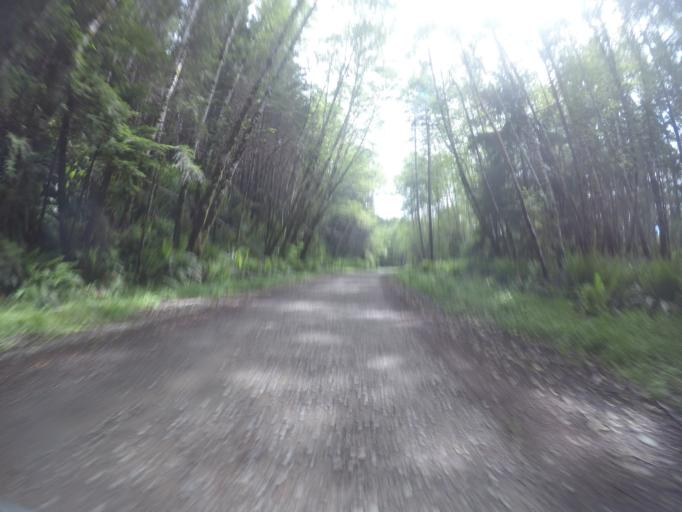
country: US
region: California
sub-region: Humboldt County
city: Westhaven-Moonstone
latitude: 41.2247
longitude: -124.0028
